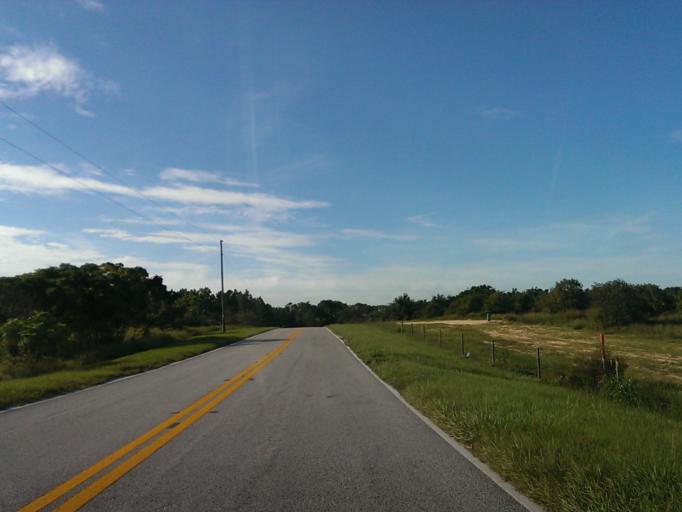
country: US
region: Florida
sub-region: Polk County
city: Citrus Ridge
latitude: 28.4109
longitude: -81.6358
